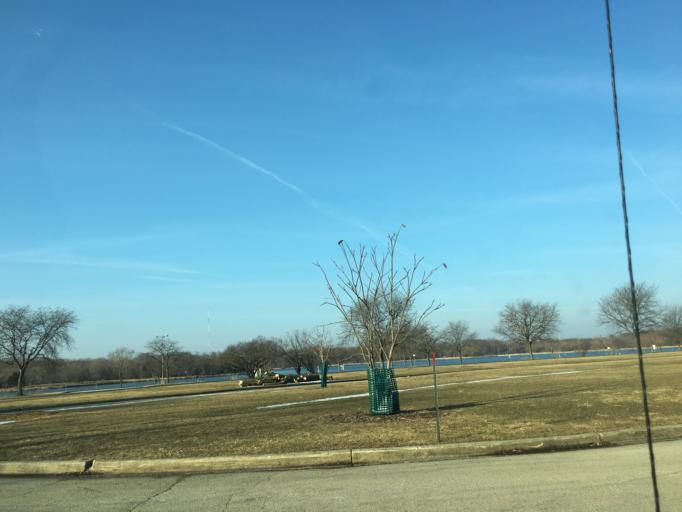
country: US
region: Illinois
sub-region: Cook County
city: Elk Grove Village
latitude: 42.0238
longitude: -88.0152
